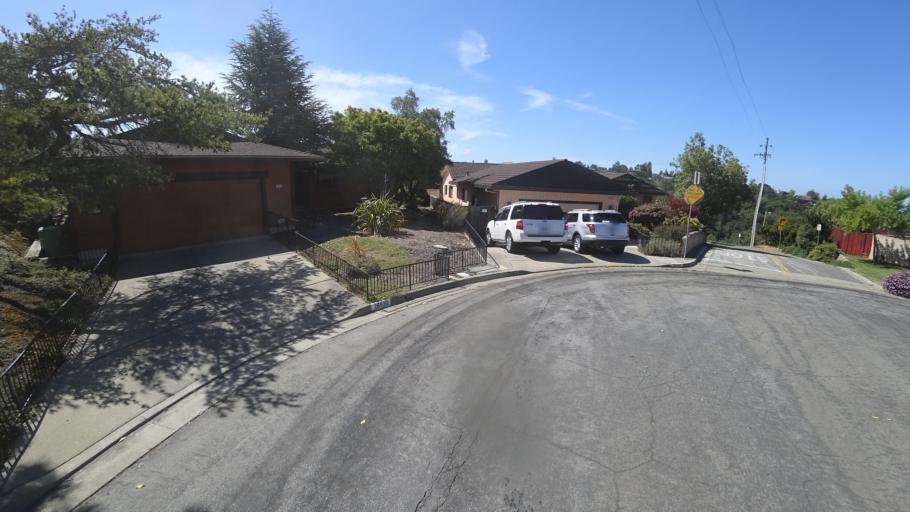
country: US
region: California
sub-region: Alameda County
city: Fairview
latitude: 37.6603
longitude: -122.0356
